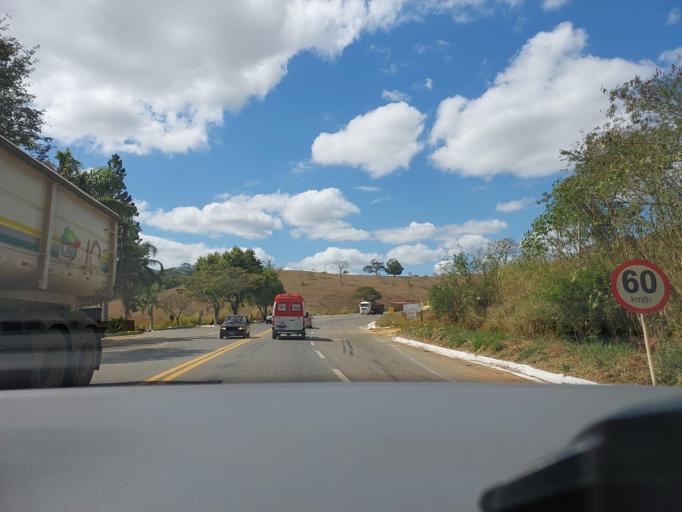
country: BR
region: Minas Gerais
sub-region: Muriae
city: Muriae
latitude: -21.1253
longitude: -42.3299
